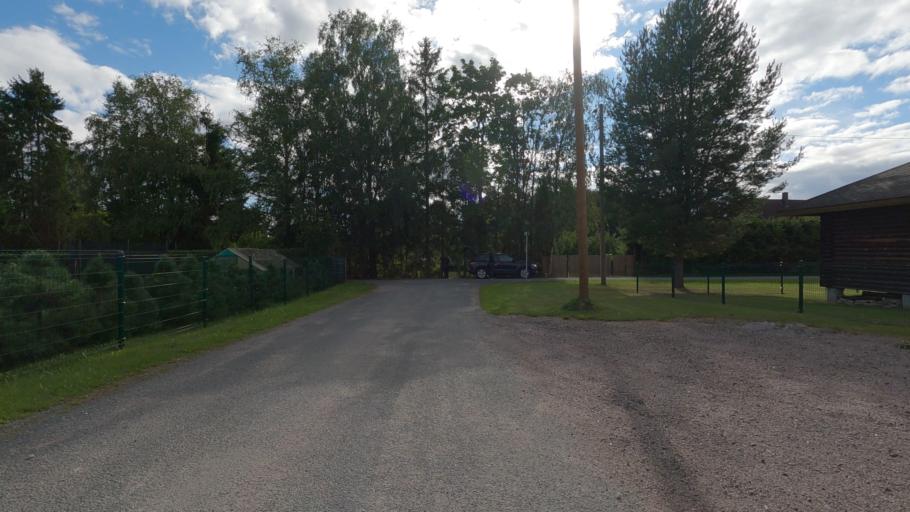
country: EE
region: Raplamaa
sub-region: Rapla vald
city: Rapla
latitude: 59.0054
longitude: 24.8033
